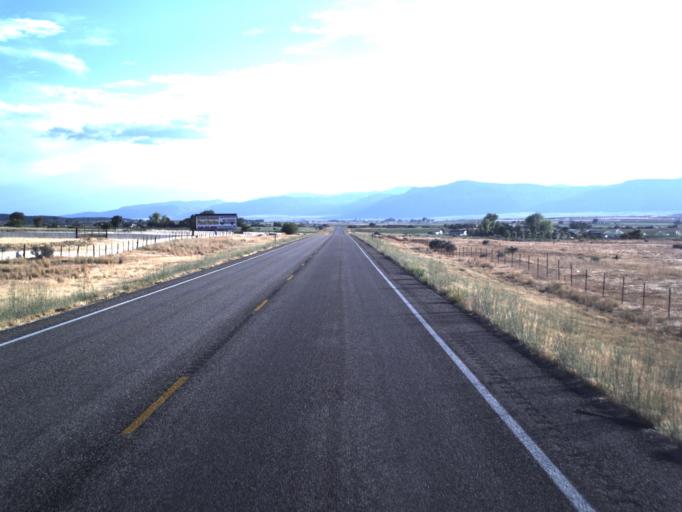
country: US
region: Utah
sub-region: Sanpete County
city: Mount Pleasant
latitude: 39.5231
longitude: -111.4773
